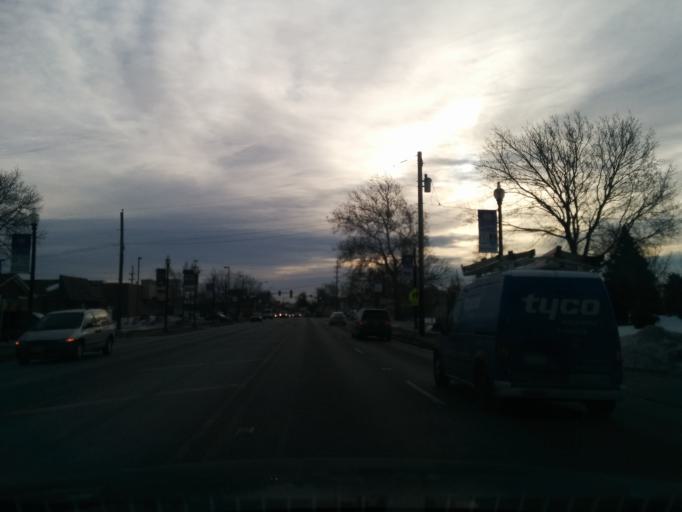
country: US
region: Illinois
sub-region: Cook County
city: Schiller Park
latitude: 41.9557
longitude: -87.8731
